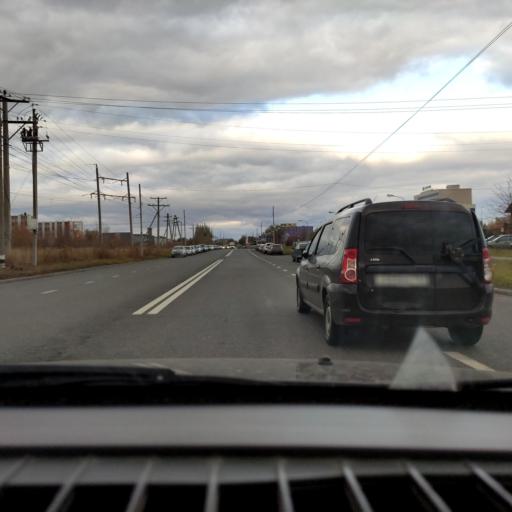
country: RU
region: Samara
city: Tol'yatti
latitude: 53.5555
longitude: 49.2939
